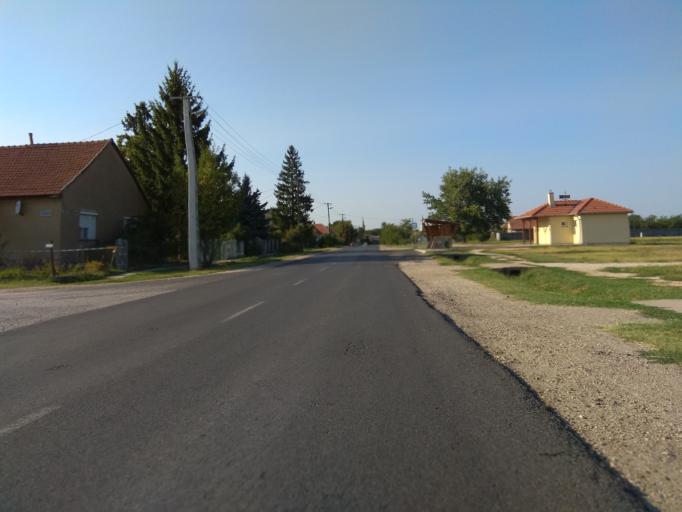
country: HU
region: Borsod-Abauj-Zemplen
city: Onod
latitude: 47.9966
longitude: 20.9206
